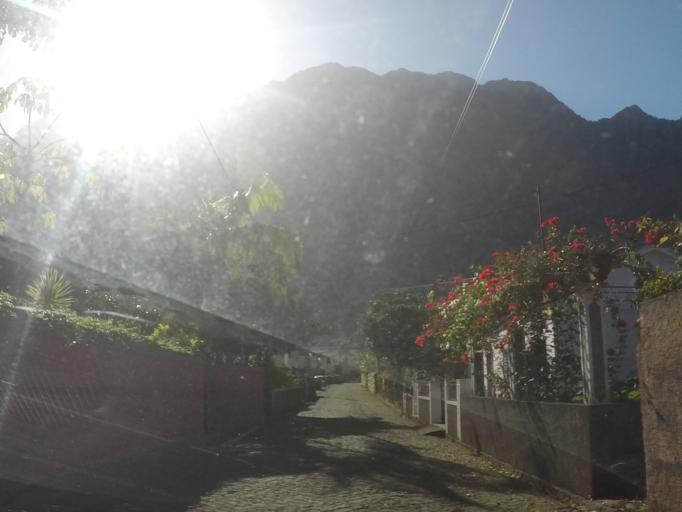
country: PT
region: Madeira
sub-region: Santana
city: Santana
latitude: 32.8276
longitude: -16.9542
